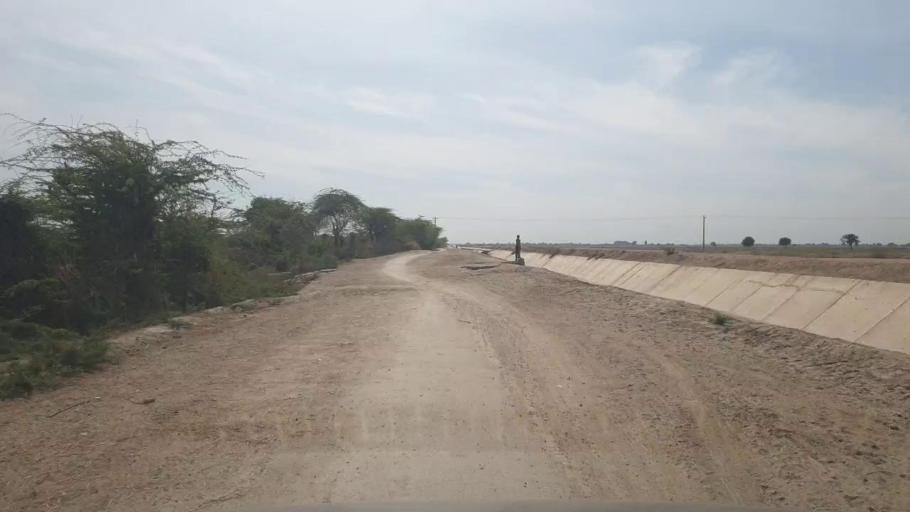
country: PK
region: Sindh
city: Umarkot
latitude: 25.3246
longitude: 69.6019
